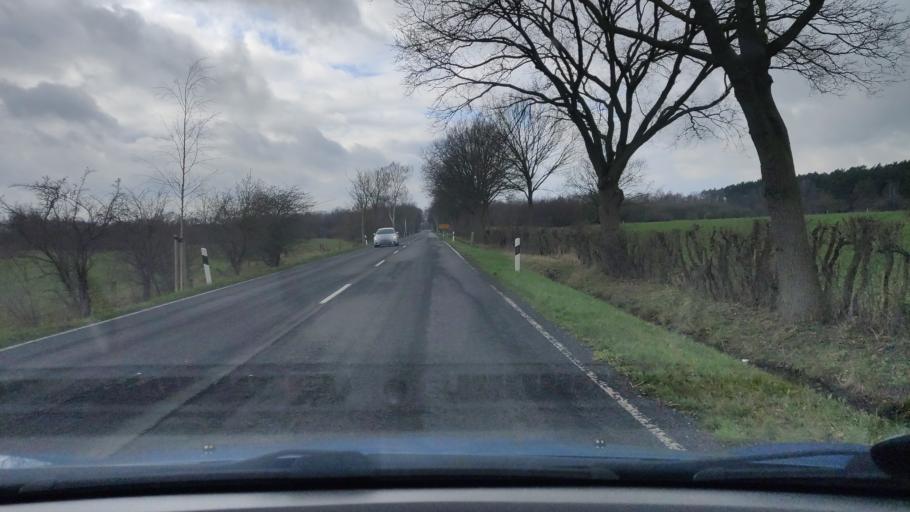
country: DE
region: Lower Saxony
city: Garbsen-Mitte
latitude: 52.4739
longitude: 9.6488
